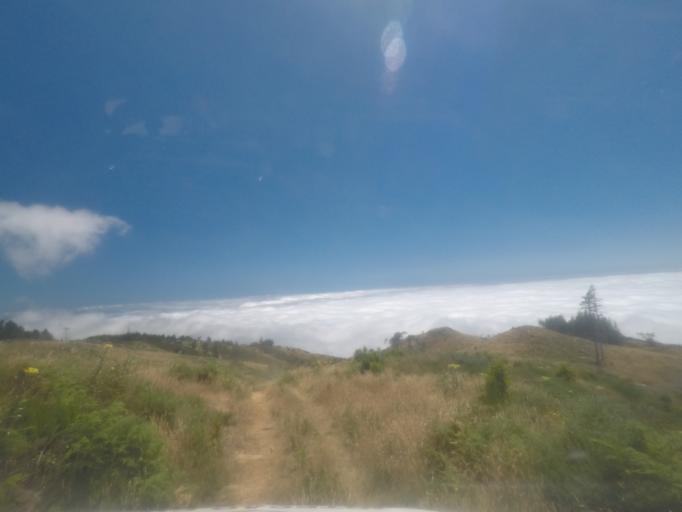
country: PT
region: Madeira
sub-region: Funchal
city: Nossa Senhora do Monte
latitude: 32.7055
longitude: -16.8977
